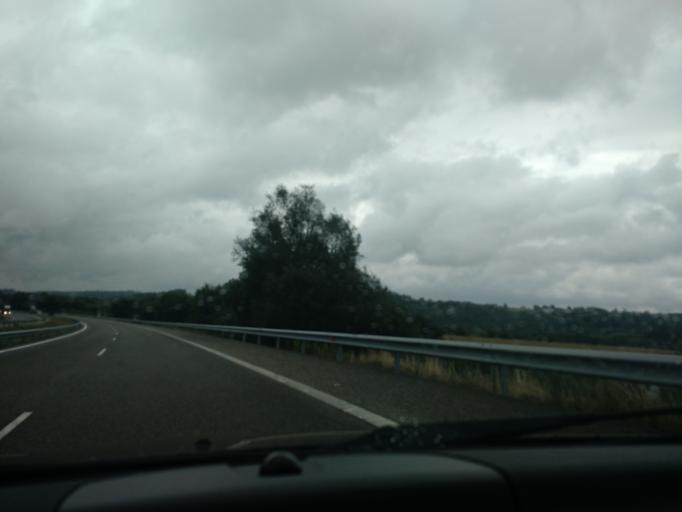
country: ES
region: Galicia
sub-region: Provincia da Coruna
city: Santiago de Compostela
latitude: 42.9143
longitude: -8.4771
